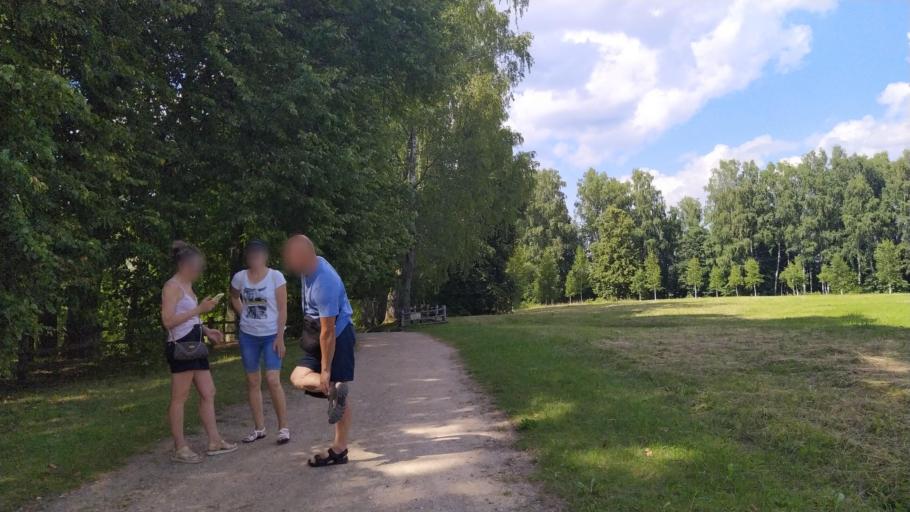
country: RU
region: Pskov
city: Pushkinskiye Gory
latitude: 57.0603
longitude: 28.9237
